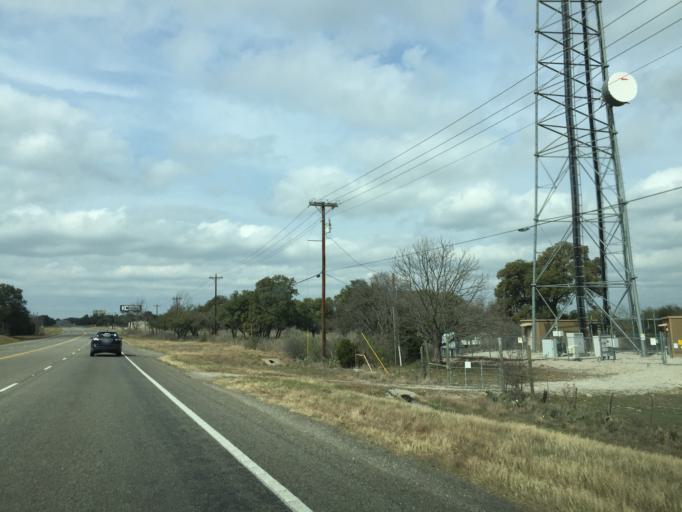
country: US
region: Texas
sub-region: Burnet County
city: Marble Falls
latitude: 30.4804
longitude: -98.1959
